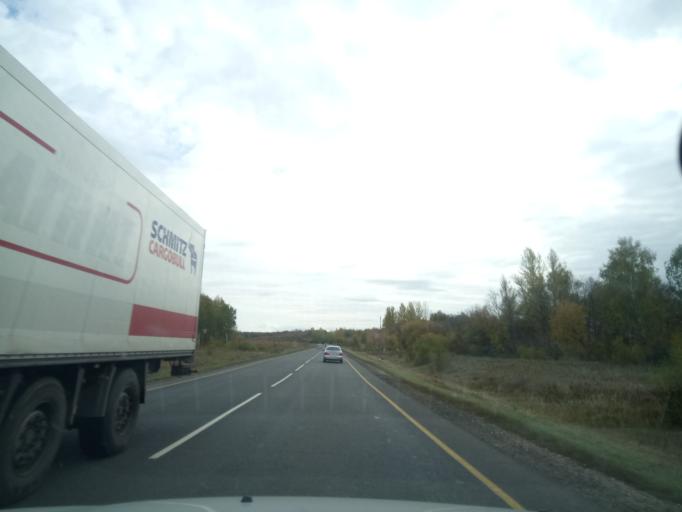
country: RU
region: Nizjnij Novgorod
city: Lukoyanov
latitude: 55.0545
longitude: 44.3708
